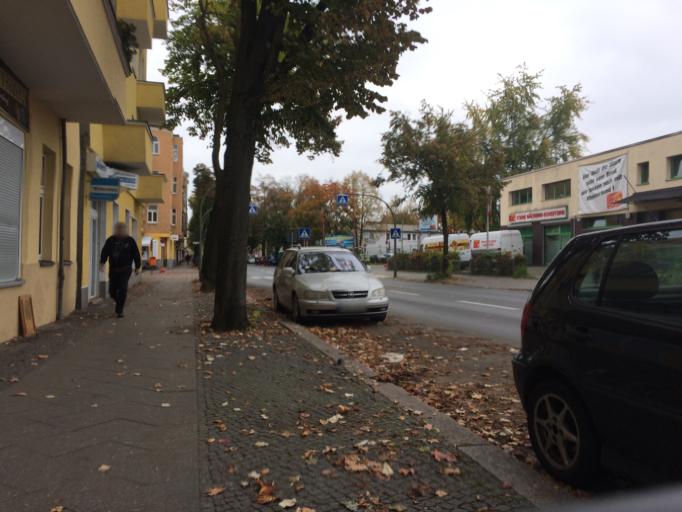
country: DE
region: Berlin
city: Gesundbrunnen
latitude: 52.5655
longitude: 13.3782
